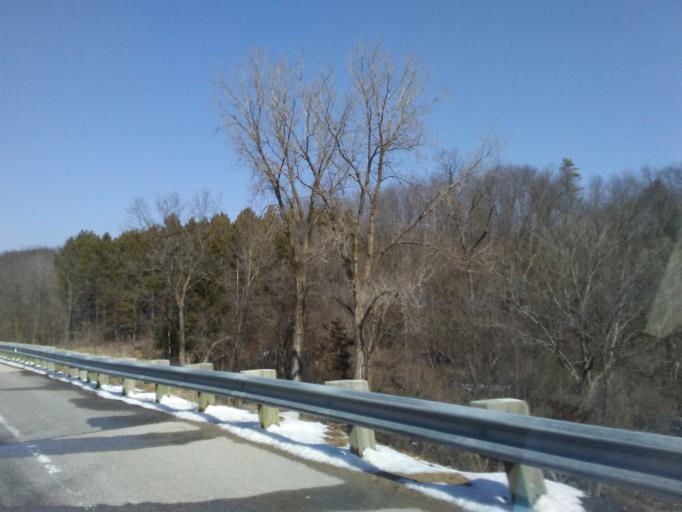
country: US
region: Wisconsin
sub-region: Vernon County
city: Viroqua
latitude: 43.4362
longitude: -90.6940
